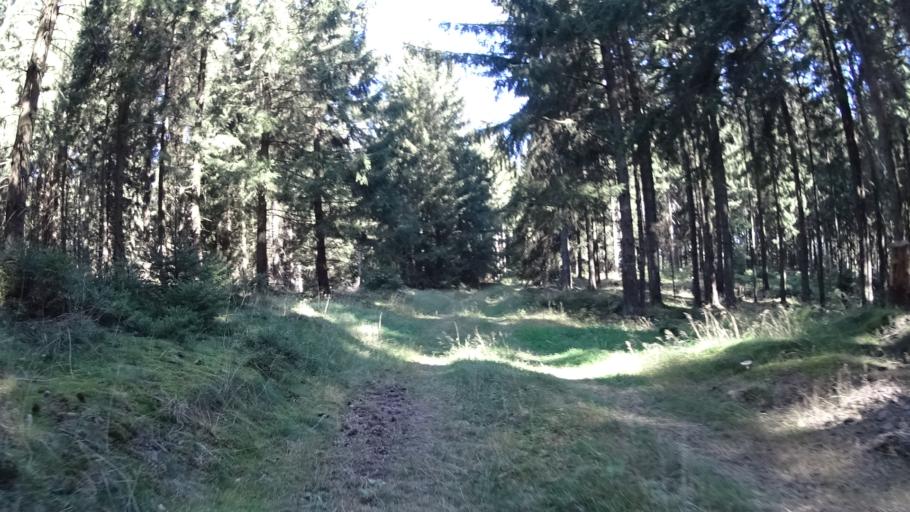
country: DE
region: Thuringia
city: Langewiesen
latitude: 50.6346
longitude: 10.9417
